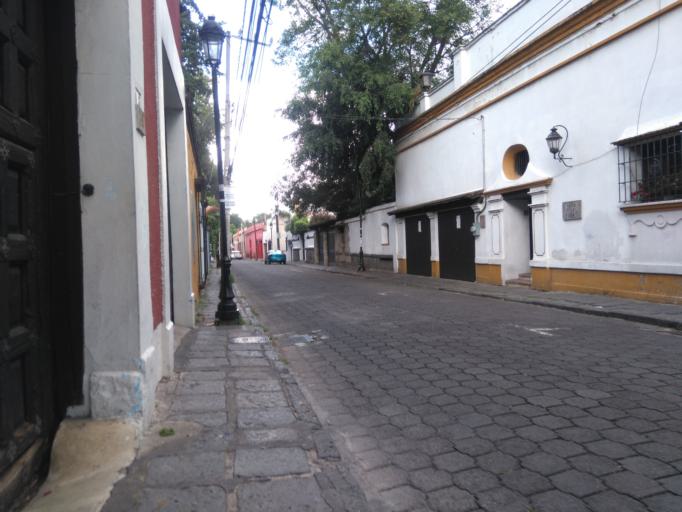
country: MX
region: Mexico City
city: Coyoacan
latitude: 19.3496
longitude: -99.1764
